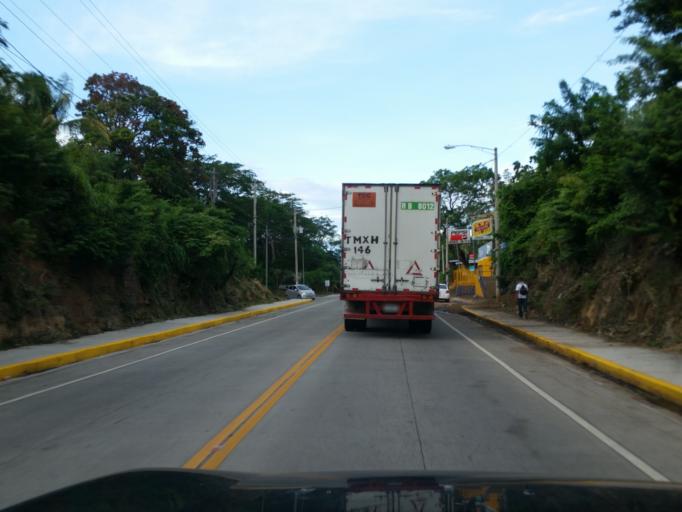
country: NI
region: Managua
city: Ciudad Sandino
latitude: 12.0948
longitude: -86.3510
